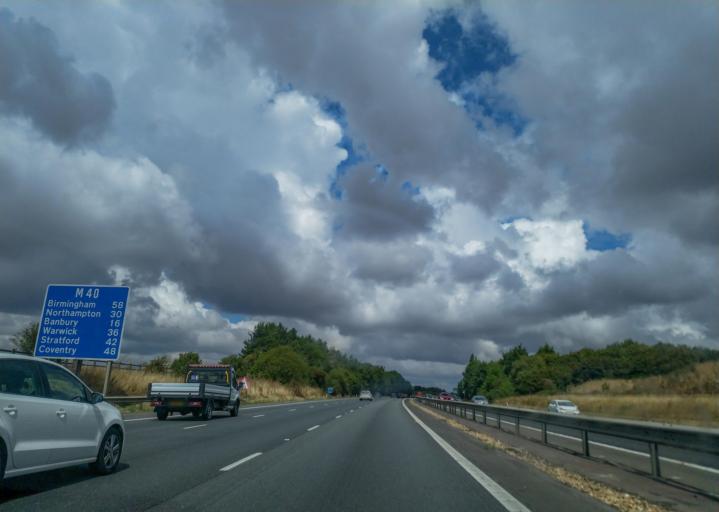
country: GB
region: England
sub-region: Oxfordshire
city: Bicester
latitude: 51.8868
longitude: -1.2050
